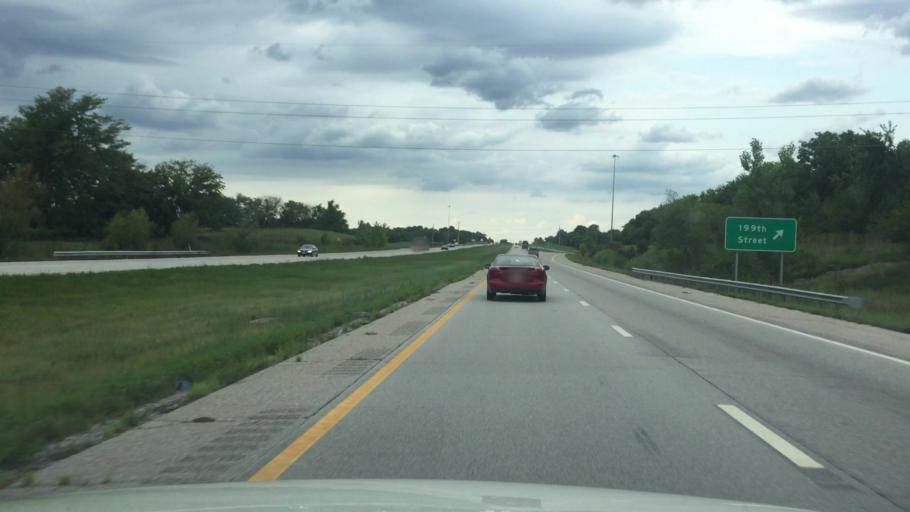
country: US
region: Kansas
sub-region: Miami County
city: Louisburg
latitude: 38.7628
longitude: -94.6776
